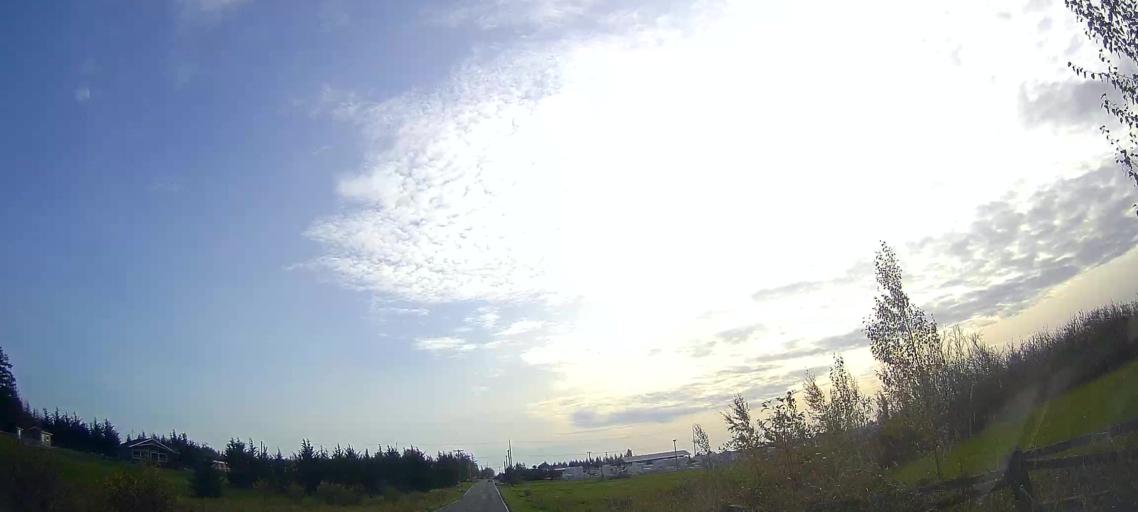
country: US
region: Washington
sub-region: Snohomish County
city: Stanwood
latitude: 48.2435
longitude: -122.4172
